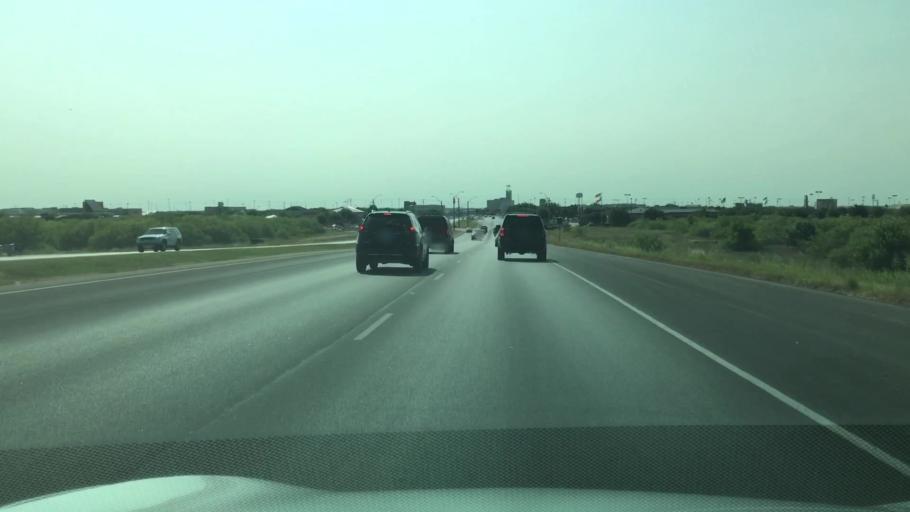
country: US
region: Texas
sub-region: Hays County
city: Kyle
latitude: 30.0166
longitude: -97.8684
